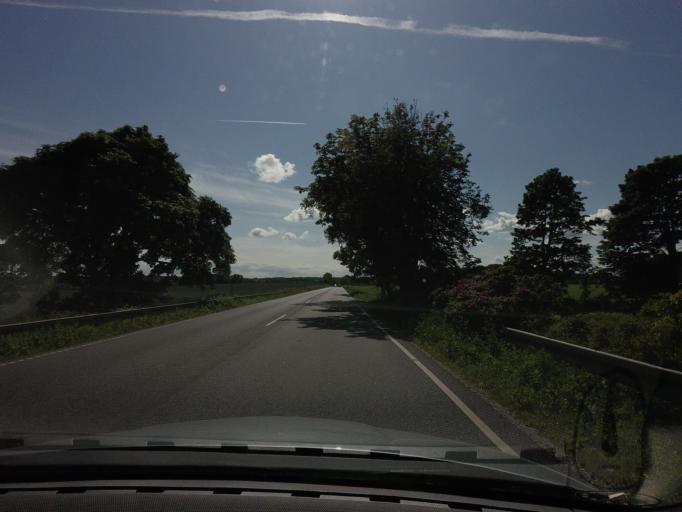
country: DK
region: Central Jutland
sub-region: Syddjurs Kommune
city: Ebeltoft
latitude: 56.3346
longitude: 10.7342
